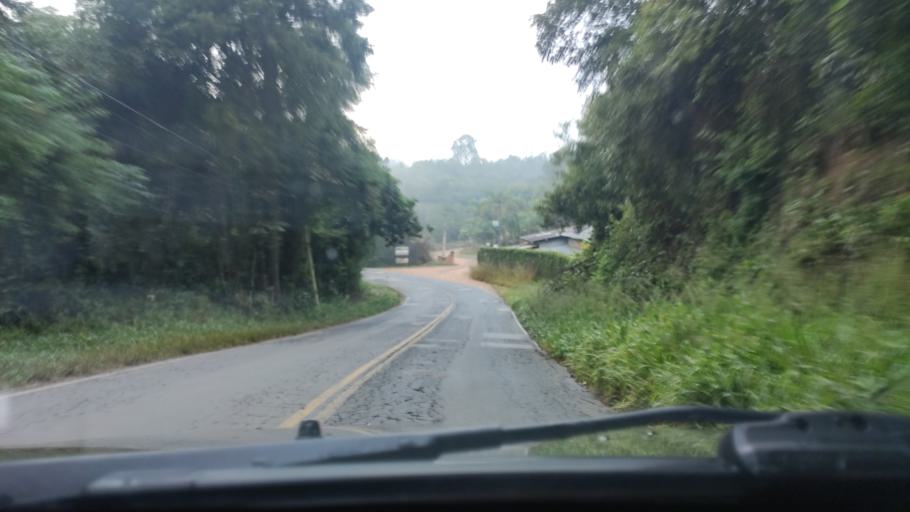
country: BR
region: Sao Paulo
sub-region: Campo Limpo Paulista
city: Campo Limpo Paulista
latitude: -23.1387
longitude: -46.7948
